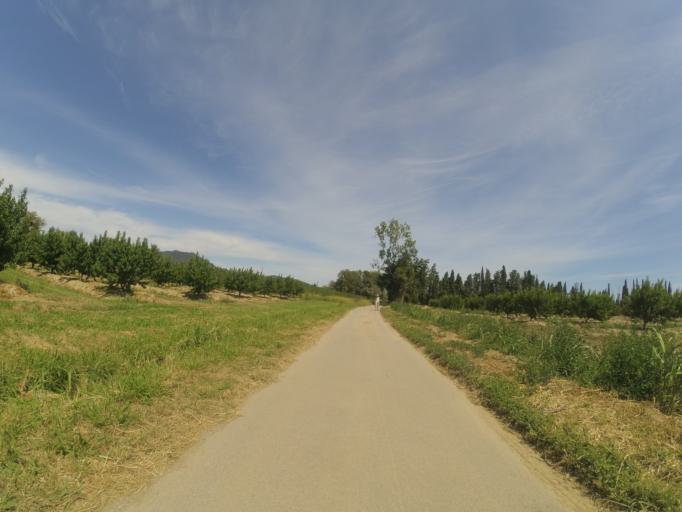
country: FR
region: Languedoc-Roussillon
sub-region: Departement des Pyrenees-Orientales
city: Millas
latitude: 42.6873
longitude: 2.6816
